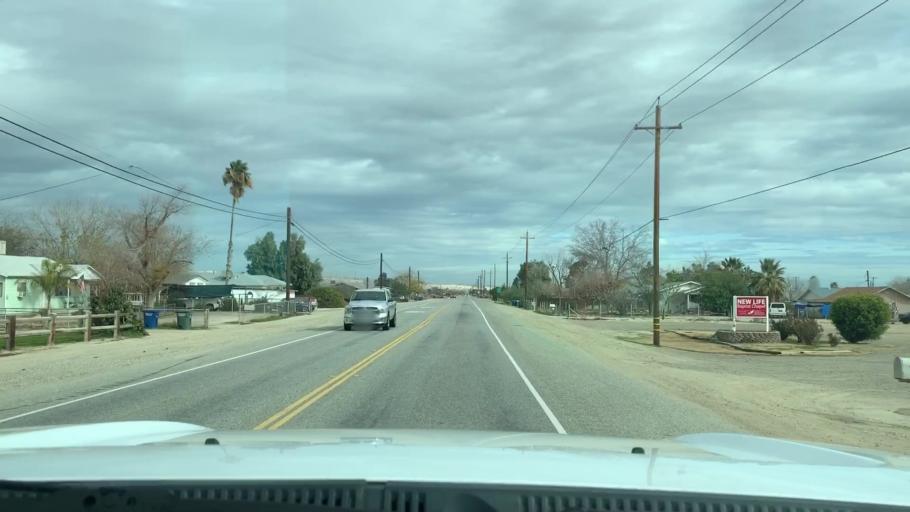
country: US
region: California
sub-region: Kern County
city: Ford City
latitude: 35.2081
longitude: -119.4074
